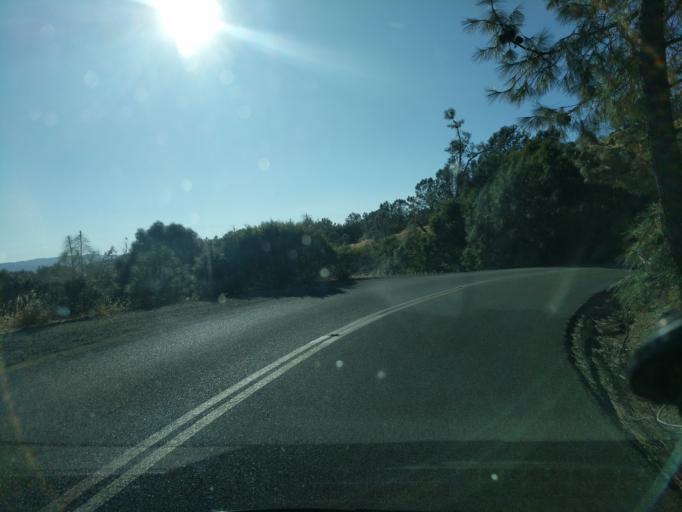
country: US
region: California
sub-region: Contra Costa County
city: Diablo
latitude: 37.8514
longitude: -121.9277
